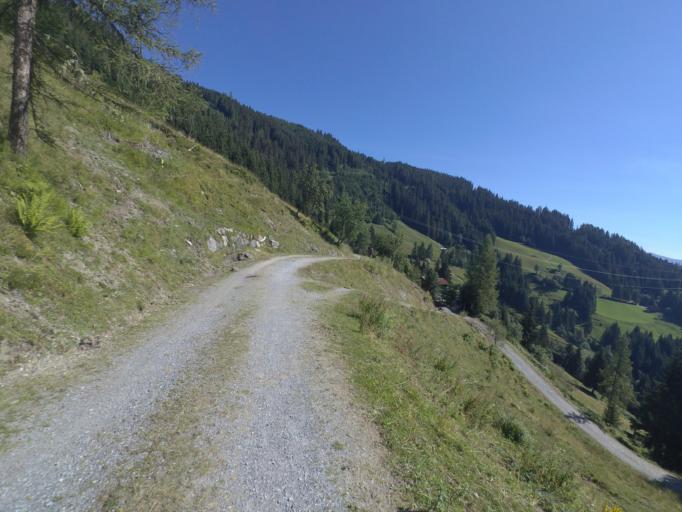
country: AT
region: Salzburg
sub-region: Politischer Bezirk Sankt Johann im Pongau
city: Muhlbach am Hochkonig
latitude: 47.3609
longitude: 13.1551
